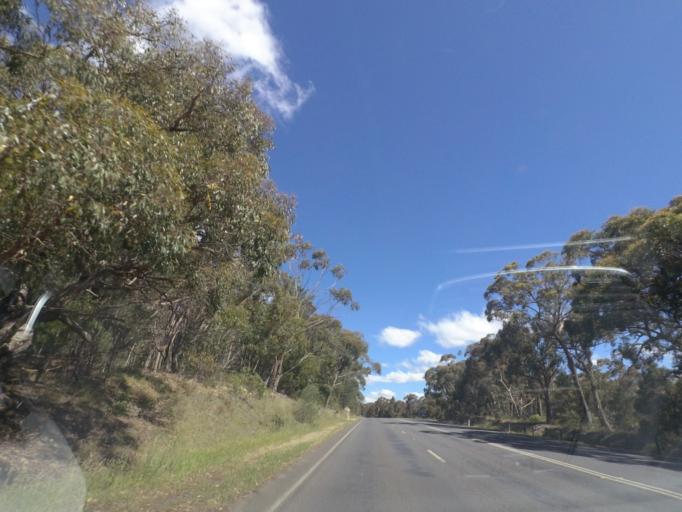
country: AU
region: Victoria
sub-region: Hume
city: Sunbury
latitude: -37.4379
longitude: 144.5645
